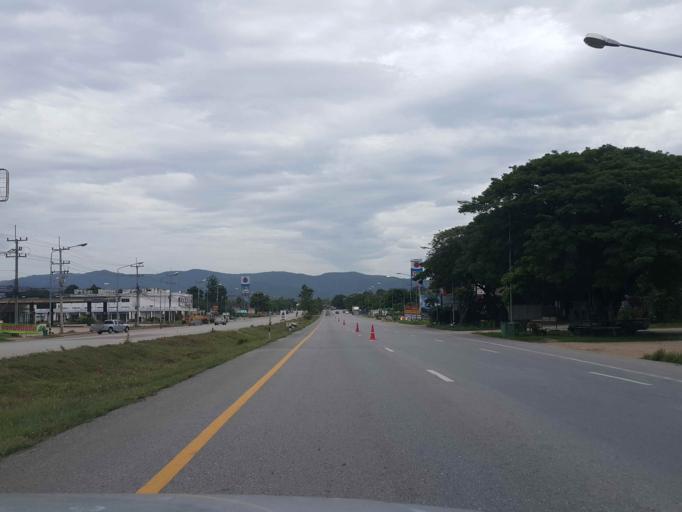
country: TH
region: Lampang
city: Thoen
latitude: 17.6164
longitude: 99.2317
